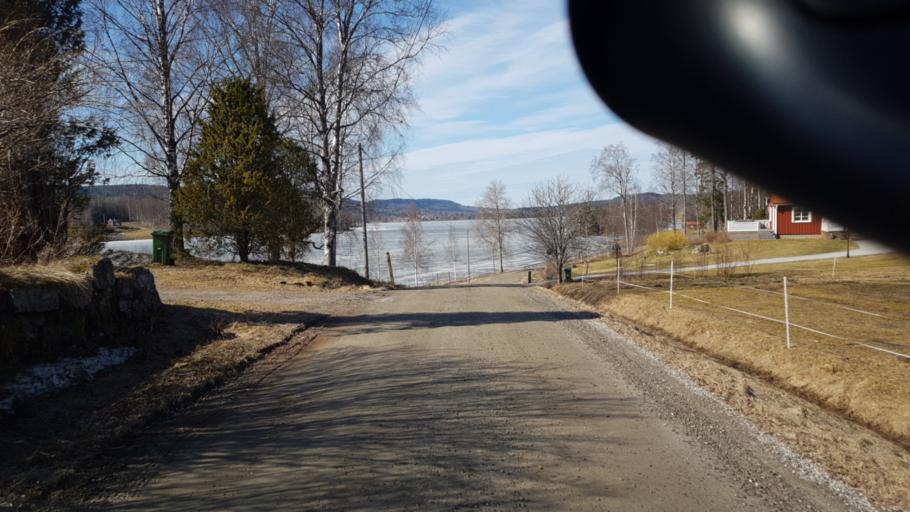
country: SE
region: Vaermland
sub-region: Arvika Kommun
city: Arvika
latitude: 59.7191
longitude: 12.8386
